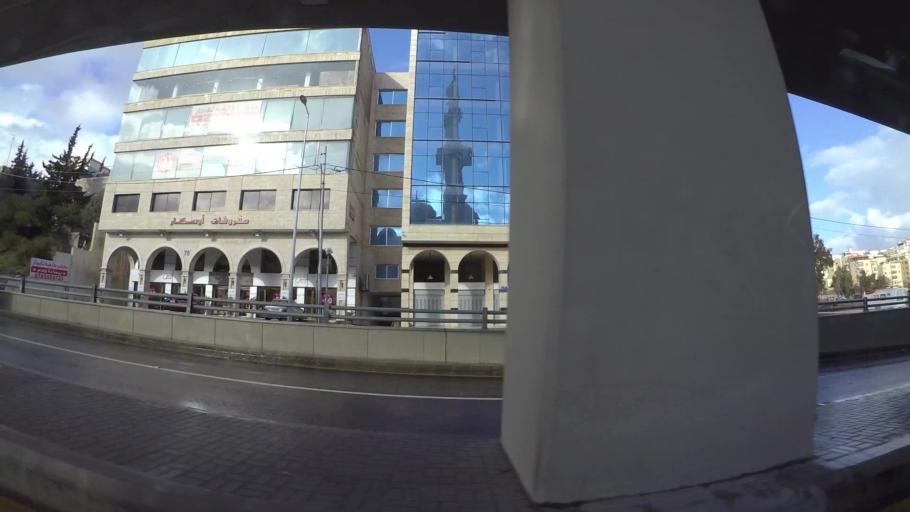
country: JO
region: Amman
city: Al Jubayhah
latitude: 31.9932
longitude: 35.8889
